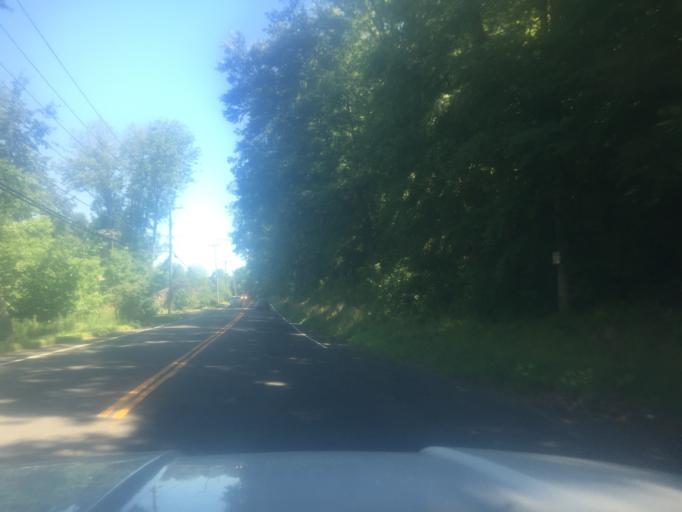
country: US
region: Connecticut
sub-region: Tolland County
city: Ellington
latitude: 41.9374
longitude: -72.4525
